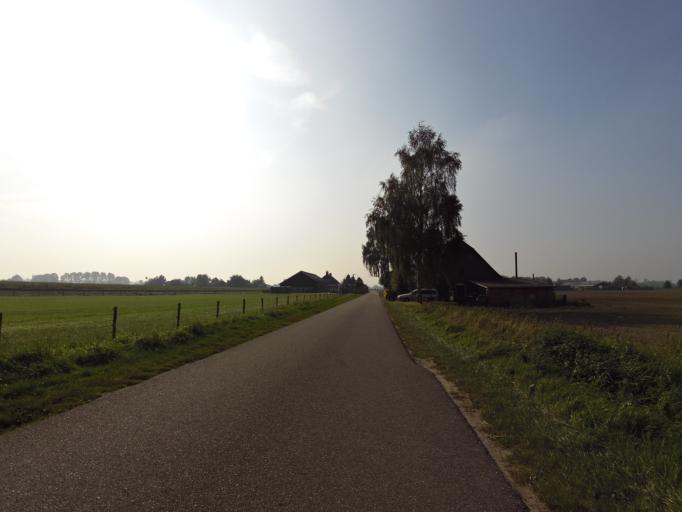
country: NL
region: Gelderland
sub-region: Gemeente Doesburg
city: Doesburg
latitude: 51.9454
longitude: 6.1714
